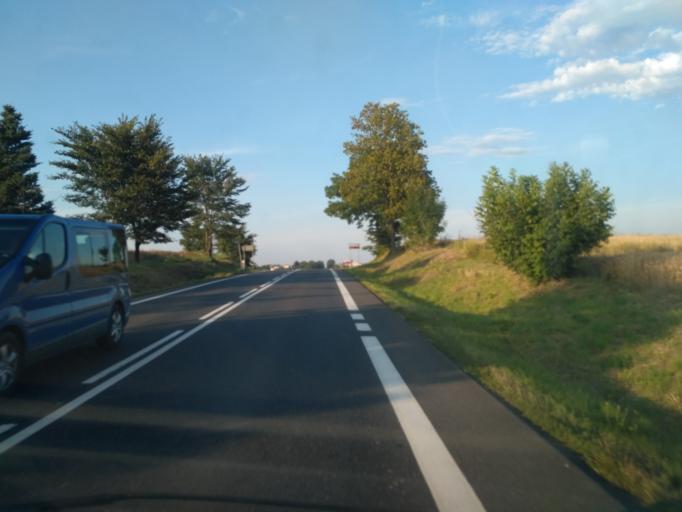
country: PL
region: Subcarpathian Voivodeship
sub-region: Powiat krosnienski
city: Miejsce Piastowe
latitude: 49.6401
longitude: 21.7979
